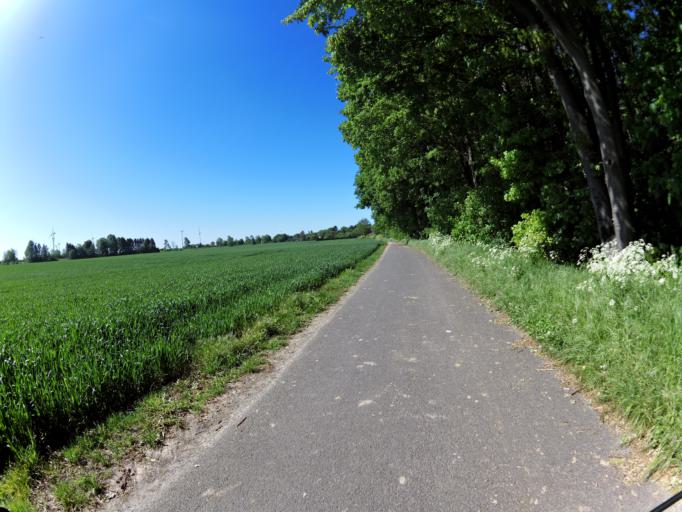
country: DE
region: North Rhine-Westphalia
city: Niedermerz
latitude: 50.8854
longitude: 6.2515
